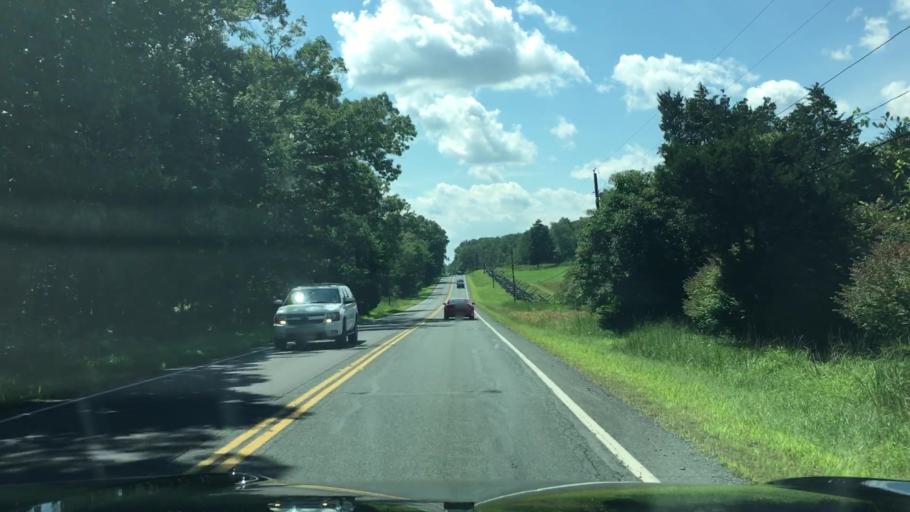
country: US
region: Virginia
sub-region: Prince William County
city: Bull Run
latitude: 38.8116
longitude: -77.5535
